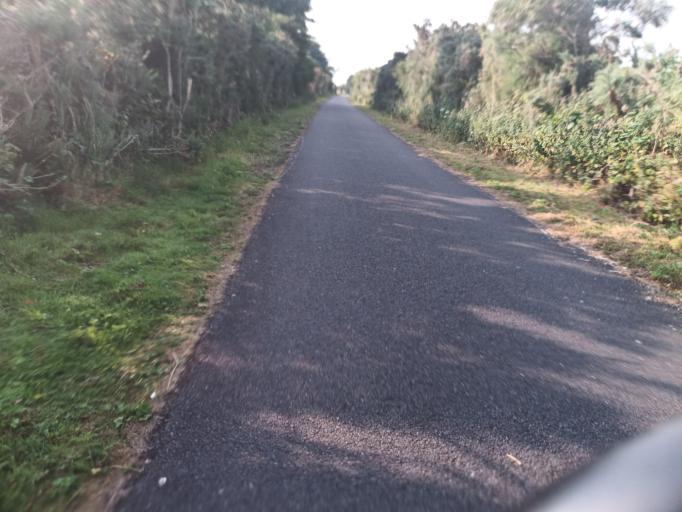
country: GB
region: Northern Ireland
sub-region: Ards District
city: Comber
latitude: 54.5656
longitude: -5.7647
